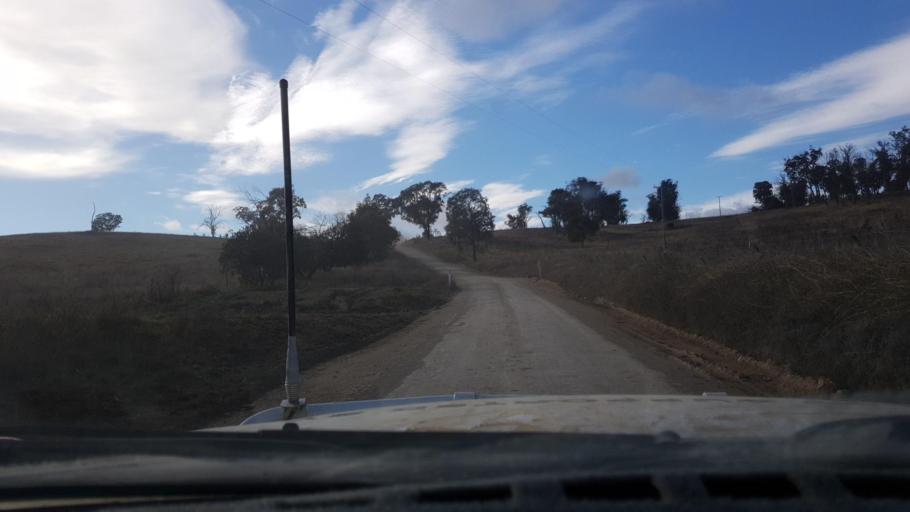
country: AU
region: New South Wales
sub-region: Armidale Dumaresq
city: Enmore
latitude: -30.7739
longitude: 151.6441
